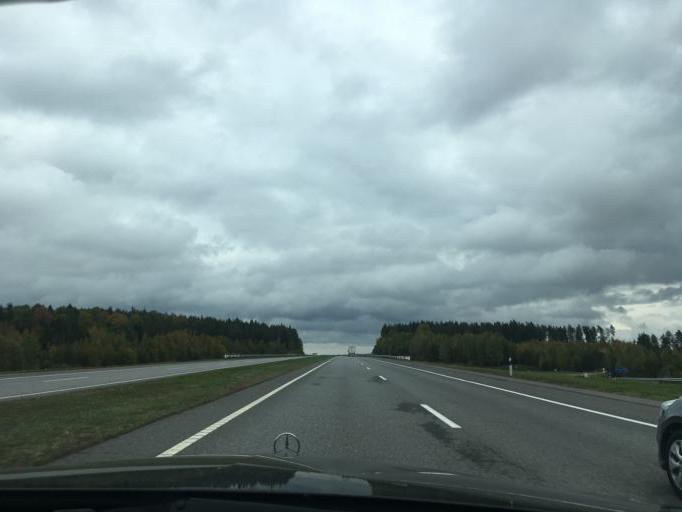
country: BY
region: Vitebsk
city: Kokhanava
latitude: 54.4779
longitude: 29.8478
